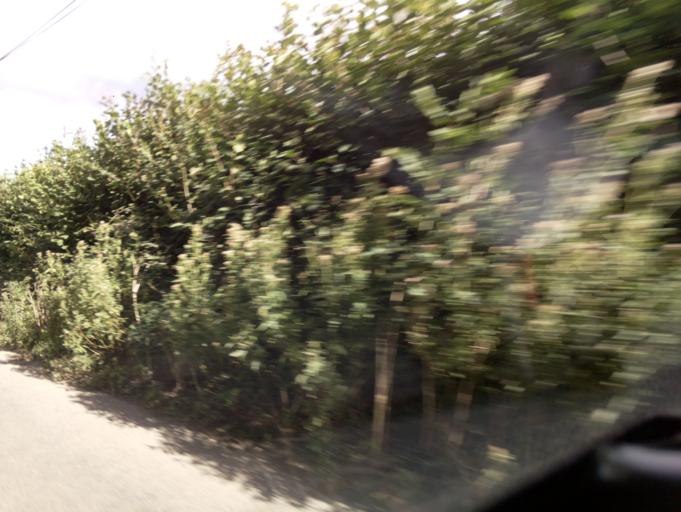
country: GB
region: England
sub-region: Devon
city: Totnes
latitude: 50.4425
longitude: -3.7276
